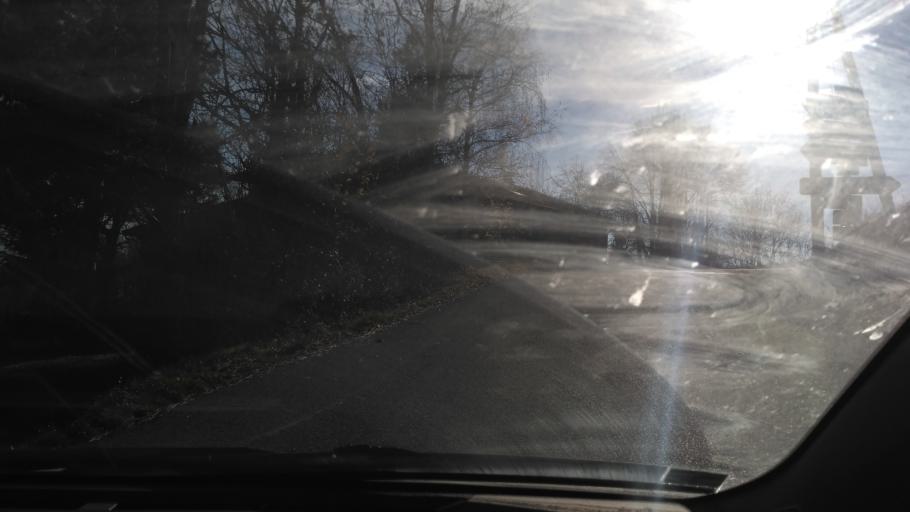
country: FR
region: Rhone-Alpes
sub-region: Departement de l'Isere
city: Saint-Antoine-l'Abbaye
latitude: 45.1726
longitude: 5.2004
